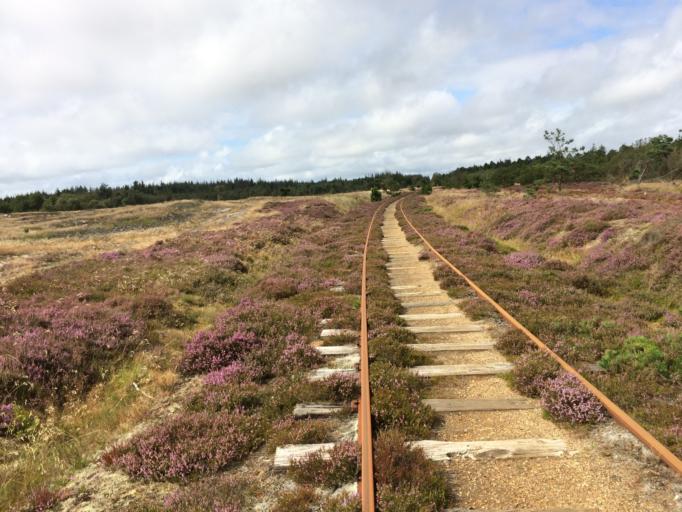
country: DK
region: South Denmark
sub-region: Varde Kommune
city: Oksbol
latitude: 55.7887
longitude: 8.2336
